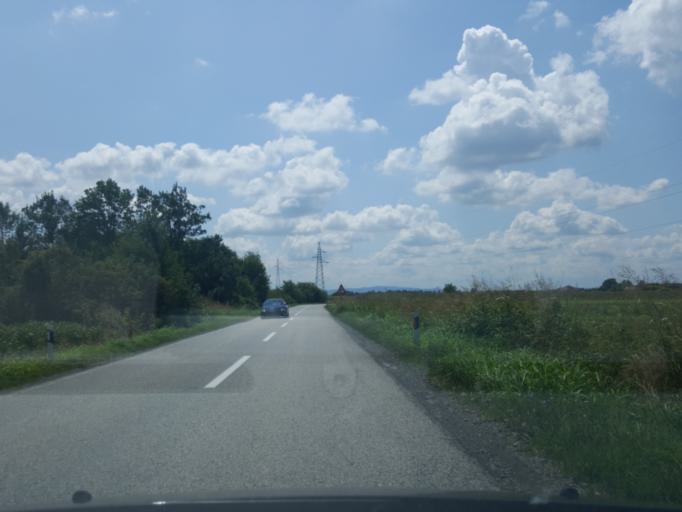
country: RS
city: Metkovic
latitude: 44.8472
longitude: 19.5207
